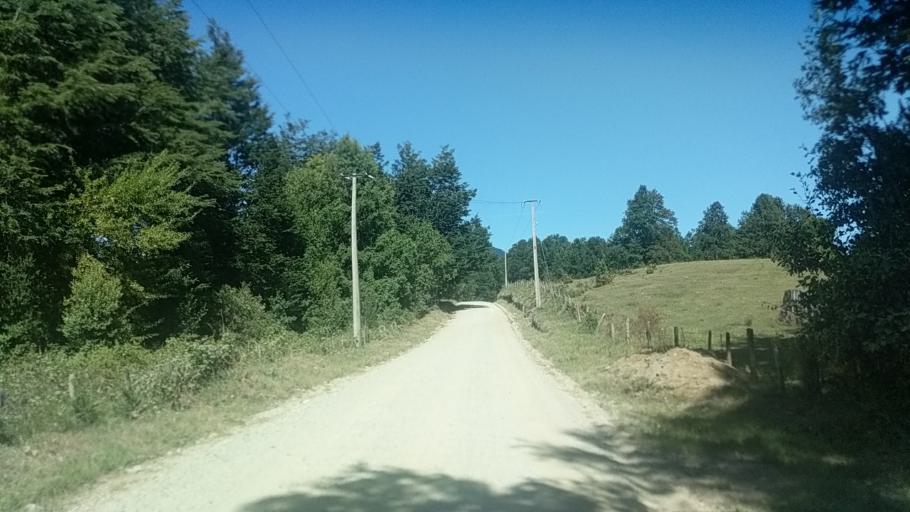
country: CL
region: Araucania
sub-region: Provincia de Cautin
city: Pucon
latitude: -39.0644
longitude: -71.7344
